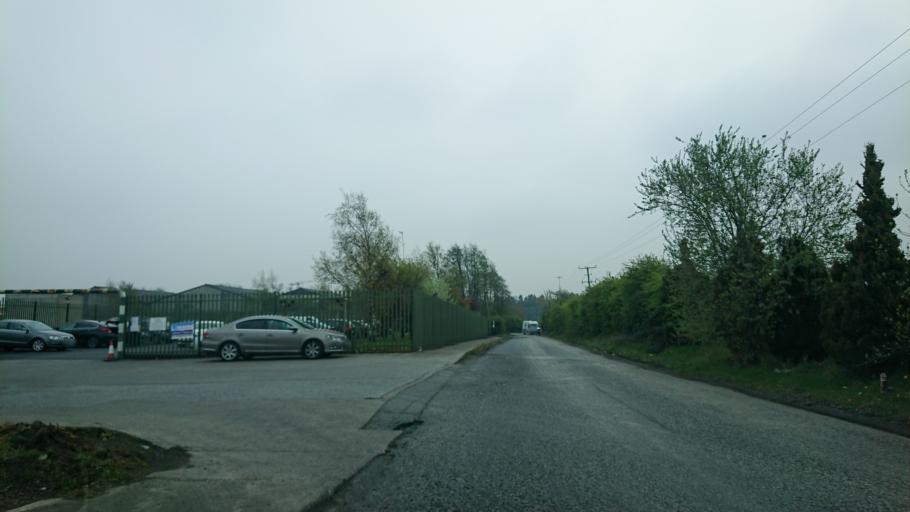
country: IE
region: Leinster
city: Ballymun
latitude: 53.4120
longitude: -6.2609
